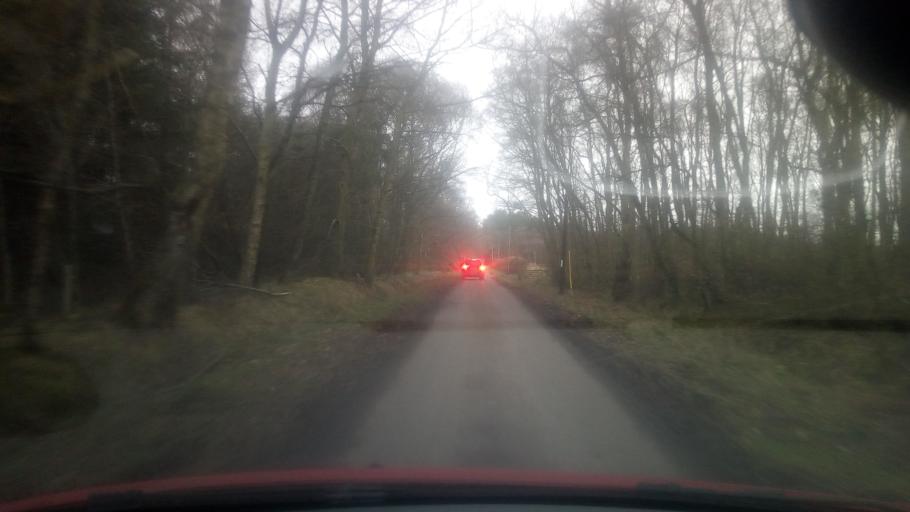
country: GB
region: Scotland
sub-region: The Scottish Borders
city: Jedburgh
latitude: 55.4649
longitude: -2.5214
